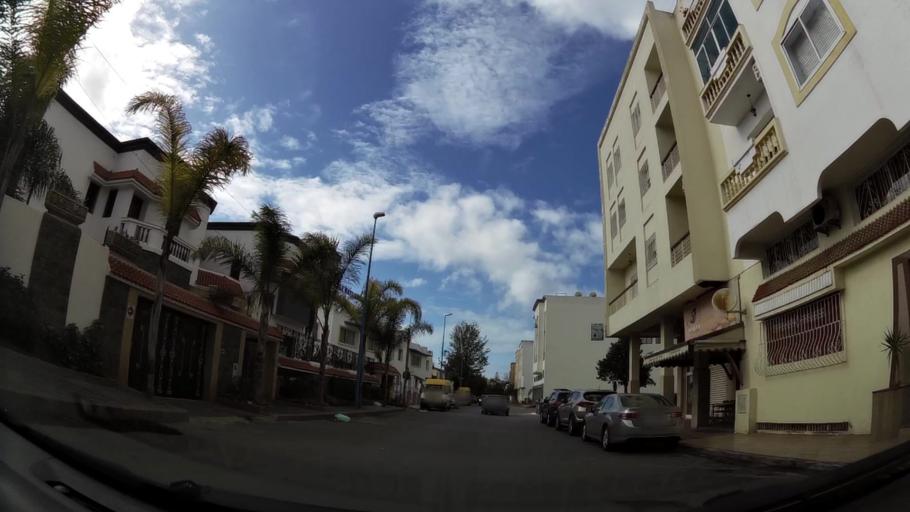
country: MA
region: Grand Casablanca
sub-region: Casablanca
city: Casablanca
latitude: 33.5438
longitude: -7.6163
